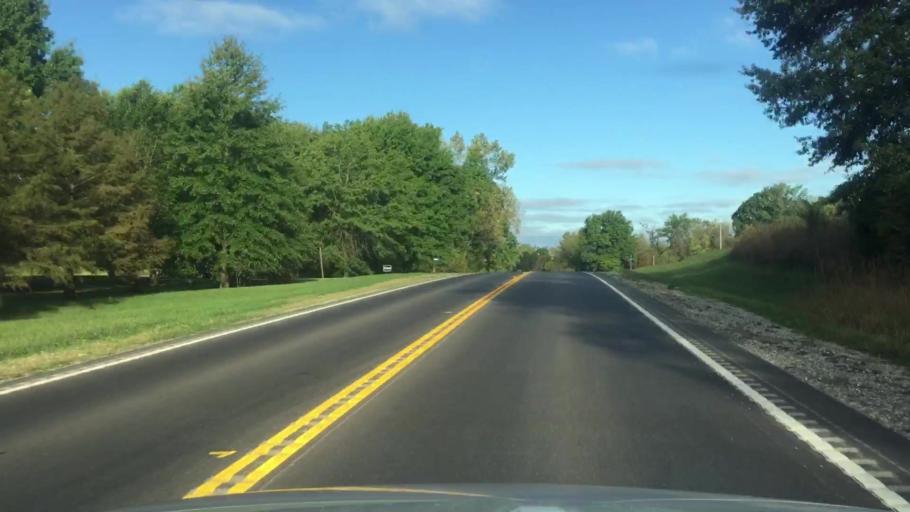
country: US
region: Missouri
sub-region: Howard County
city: New Franklin
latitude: 38.9910
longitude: -92.5614
